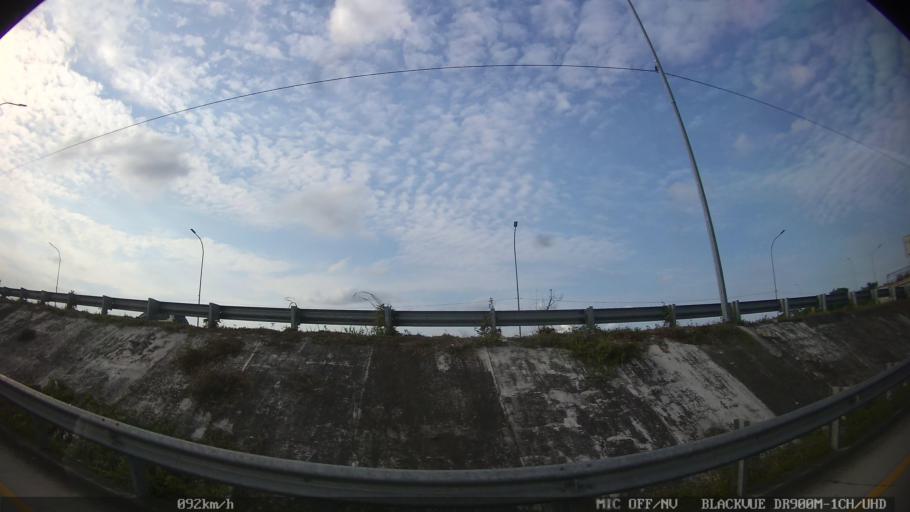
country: ID
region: North Sumatra
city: Medan
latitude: 3.6384
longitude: 98.6428
